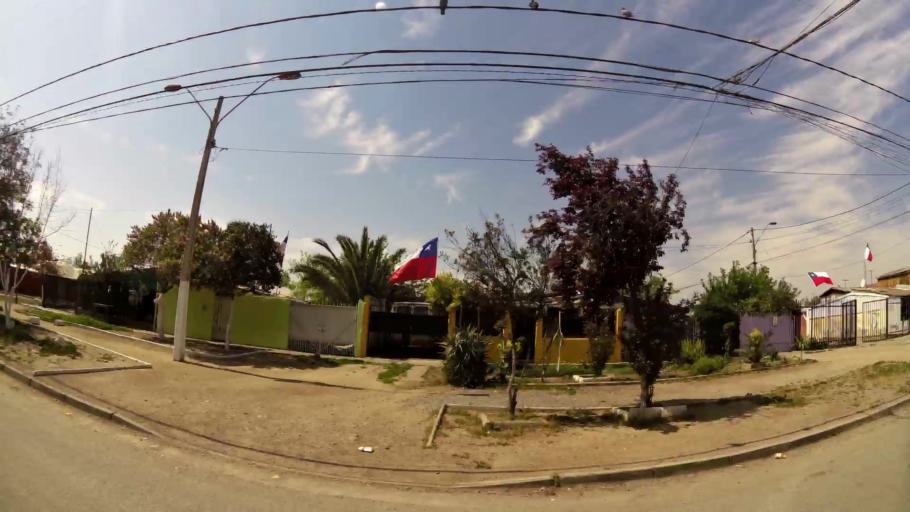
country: CL
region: Santiago Metropolitan
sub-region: Provincia de Santiago
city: La Pintana
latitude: -33.5484
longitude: -70.6489
